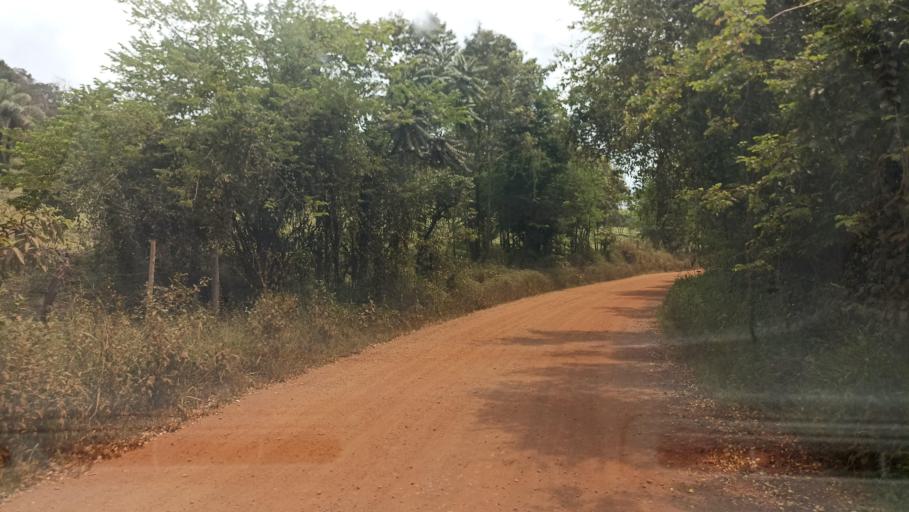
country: BR
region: Minas Gerais
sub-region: Itabirito
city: Itabirito
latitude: -20.3485
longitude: -43.7423
